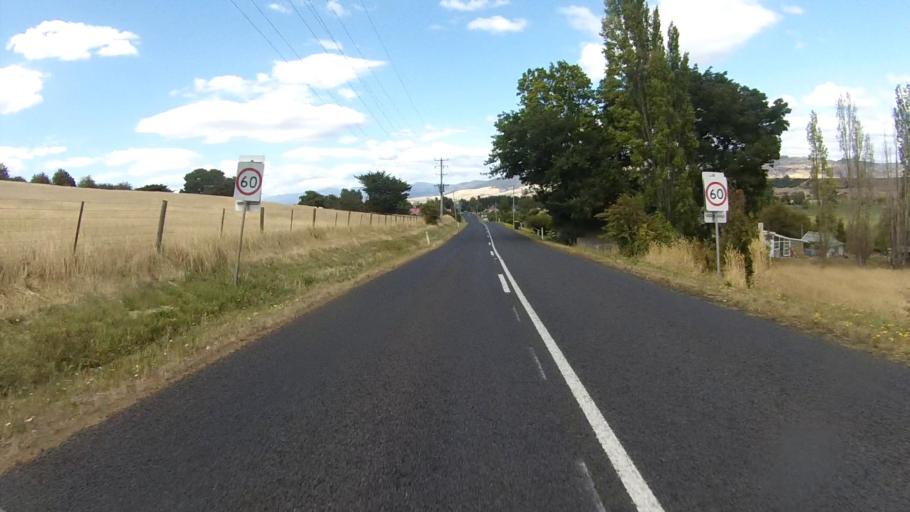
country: AU
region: Tasmania
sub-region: Derwent Valley
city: New Norfolk
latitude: -42.6932
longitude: 146.8860
